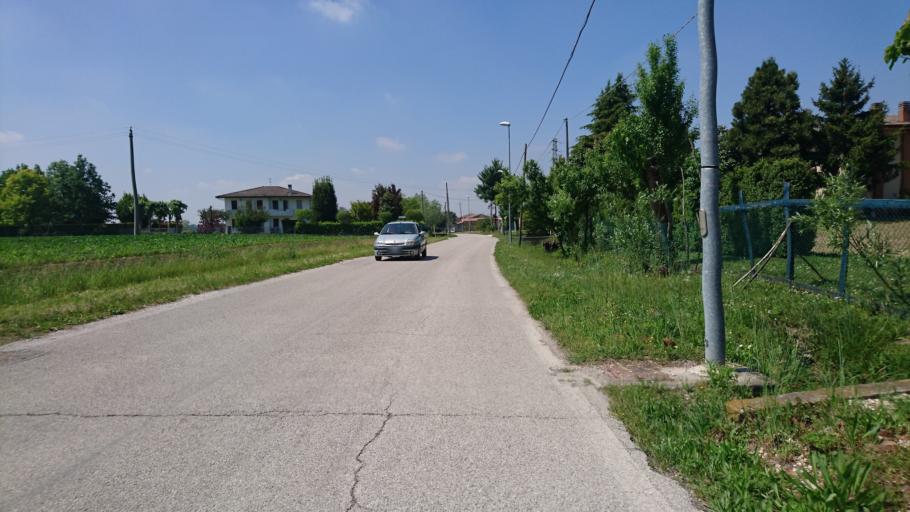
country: IT
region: Veneto
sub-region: Provincia di Padova
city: Casalserugo
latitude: 45.3032
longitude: 11.9134
